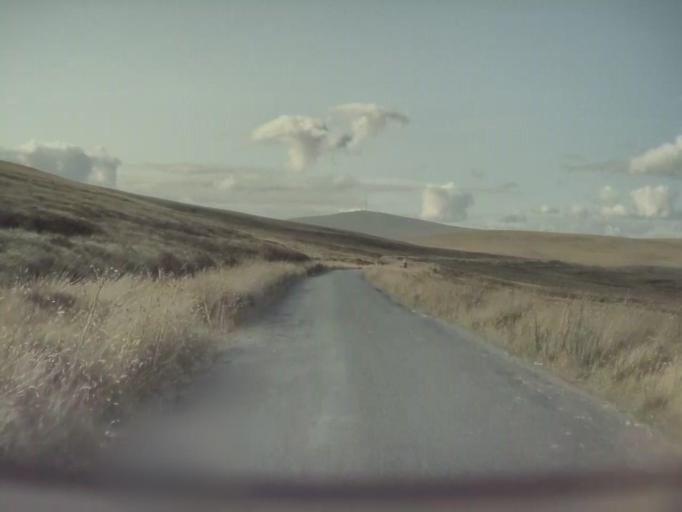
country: IE
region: Leinster
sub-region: Wicklow
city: Enniskerry
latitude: 53.1225
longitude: -6.3035
